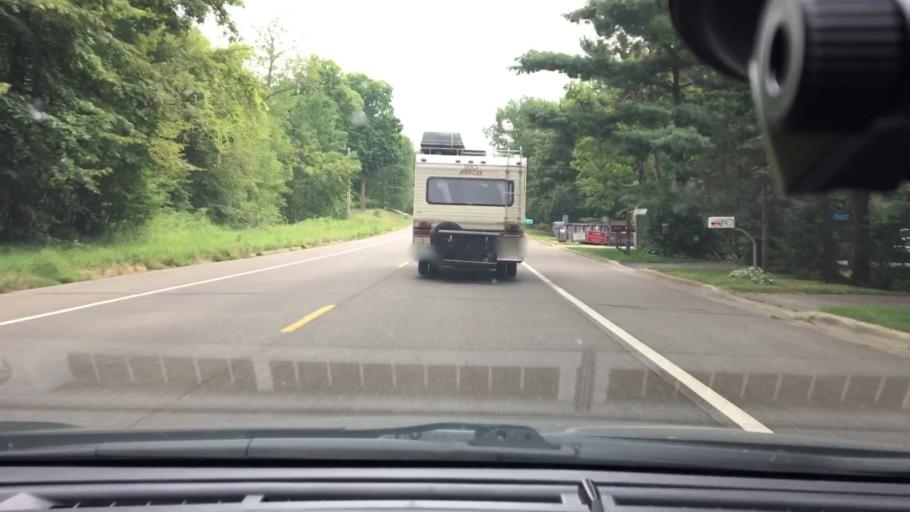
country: US
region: Minnesota
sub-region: Crow Wing County
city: Crosby
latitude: 46.4104
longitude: -93.8594
